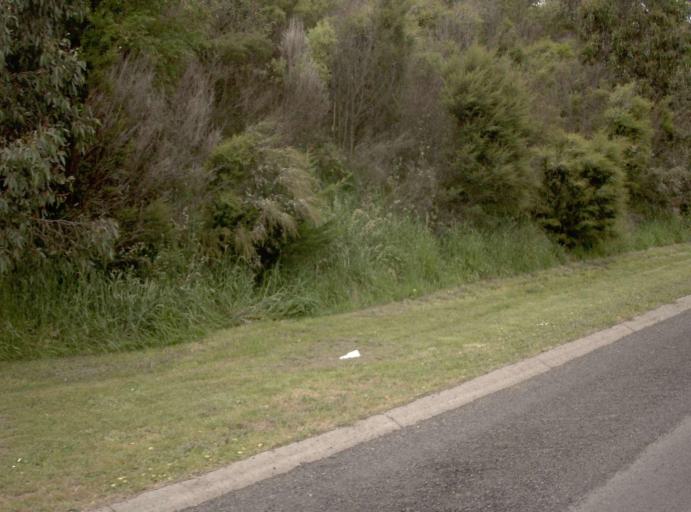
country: AU
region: Victoria
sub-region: Bass Coast
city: North Wonthaggi
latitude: -38.4009
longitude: 145.7579
